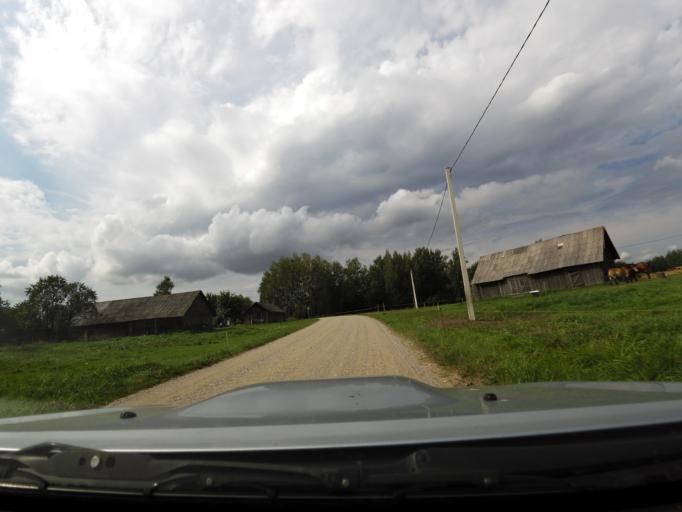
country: LT
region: Vilnius County
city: Elektrenai
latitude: 54.9184
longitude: 24.7350
